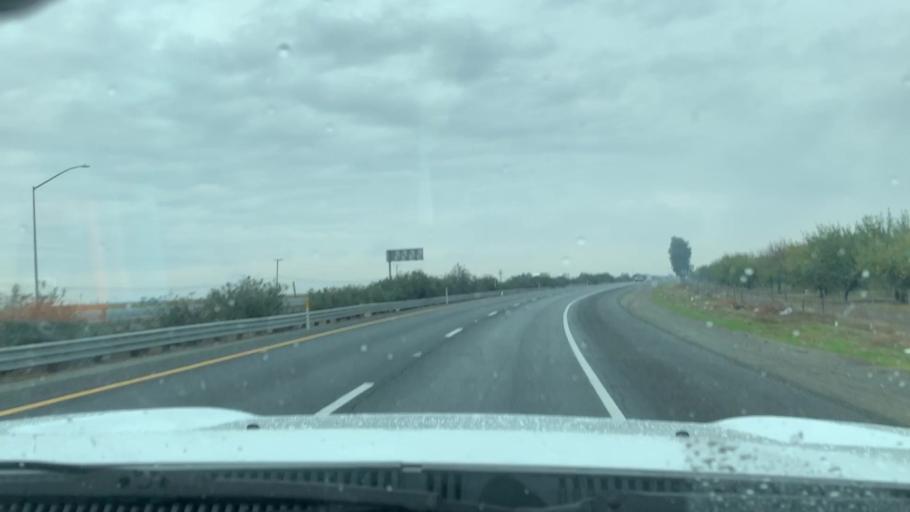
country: US
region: California
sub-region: Kern County
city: Delano
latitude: 35.7938
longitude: -119.2529
